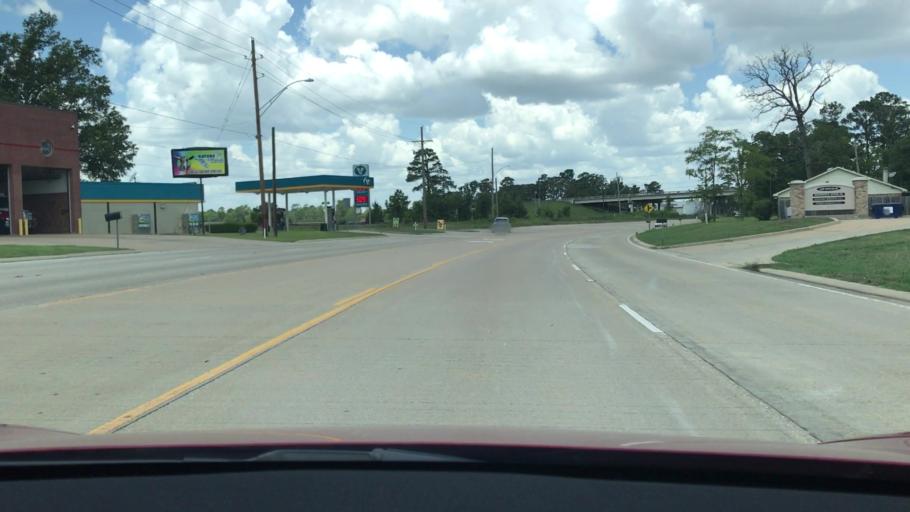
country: US
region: Louisiana
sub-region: Bossier Parish
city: Bossier City
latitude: 32.3988
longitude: -93.7332
